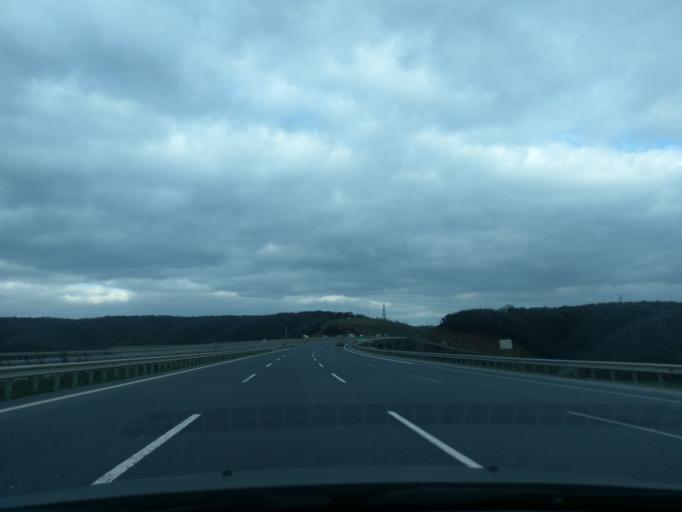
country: TR
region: Istanbul
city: Basaksehir
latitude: 41.1681
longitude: 28.8090
